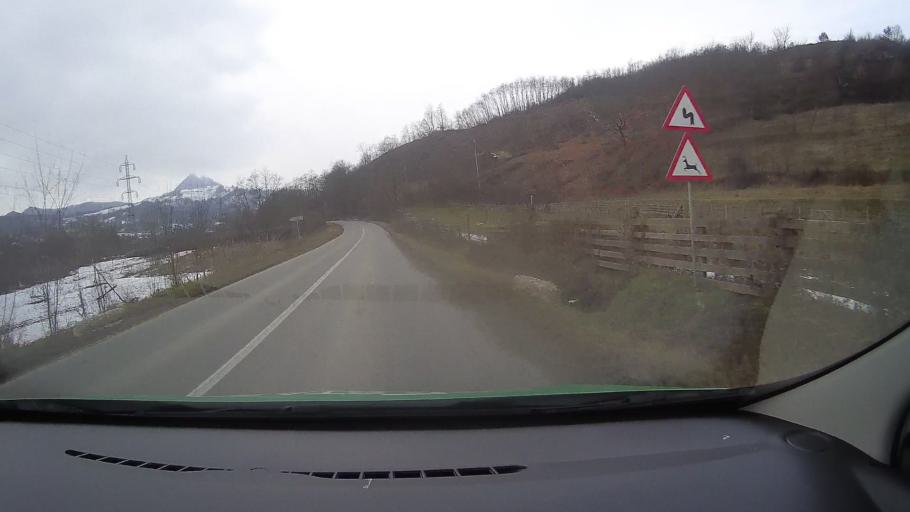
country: RO
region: Alba
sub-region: Oras Zlatna
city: Fenes
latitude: 46.0909
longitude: 23.2788
